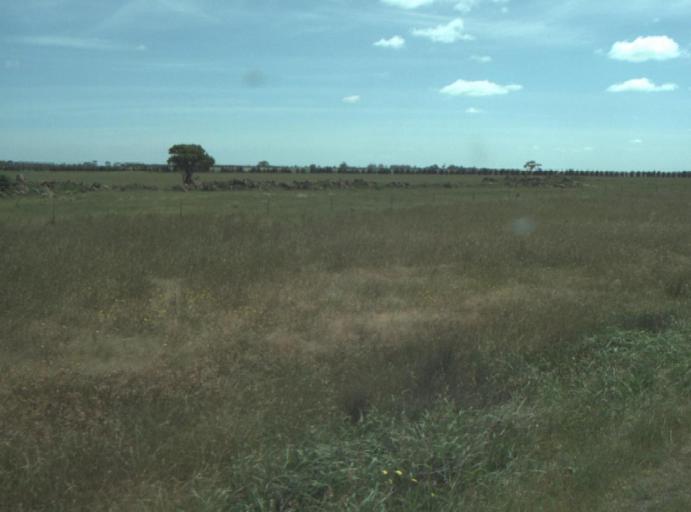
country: AU
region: Victoria
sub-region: Wyndham
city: Little River
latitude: -38.0067
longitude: 144.4640
